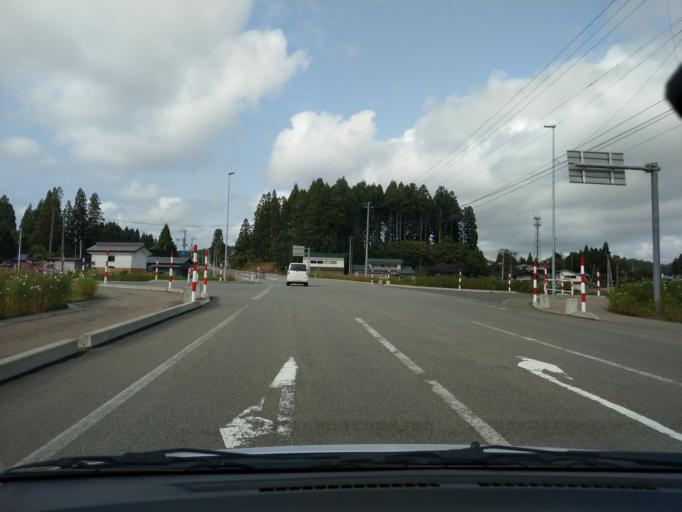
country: JP
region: Akita
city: Omagari
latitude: 39.4383
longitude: 140.3617
